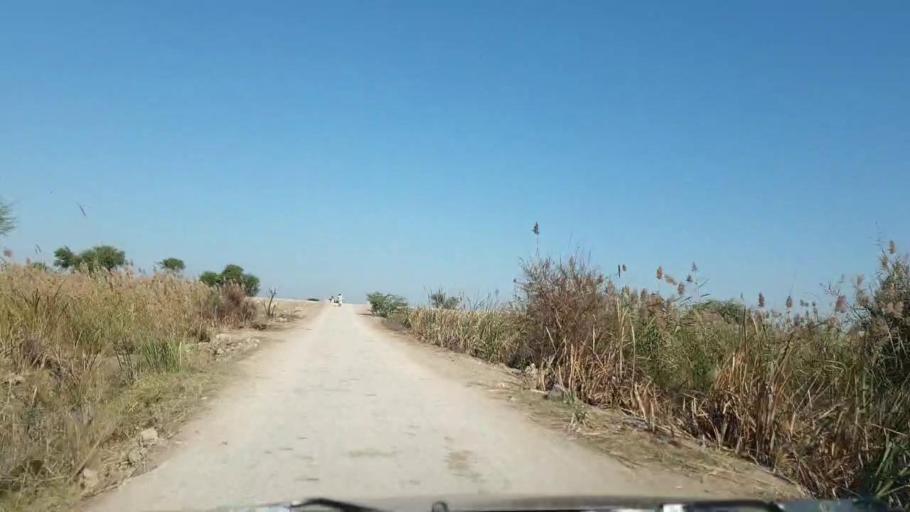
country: PK
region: Sindh
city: Sinjhoro
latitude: 26.1048
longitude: 68.8427
